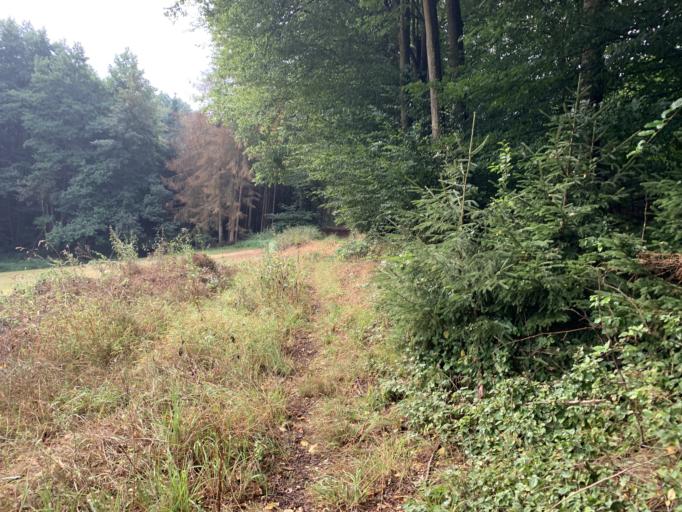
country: DE
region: Rheinland-Pfalz
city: Holzhausen an der Haide
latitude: 50.2190
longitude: 7.9216
